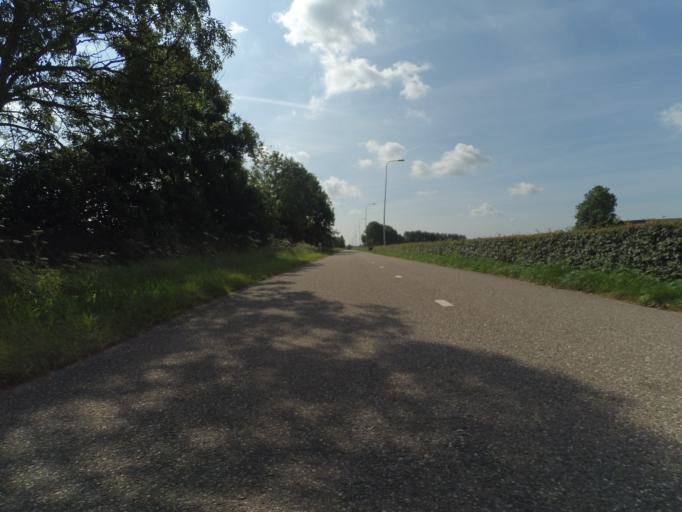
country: NL
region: Utrecht
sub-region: Gemeente Bunnik
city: Bunnik
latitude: 52.0425
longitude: 5.2315
